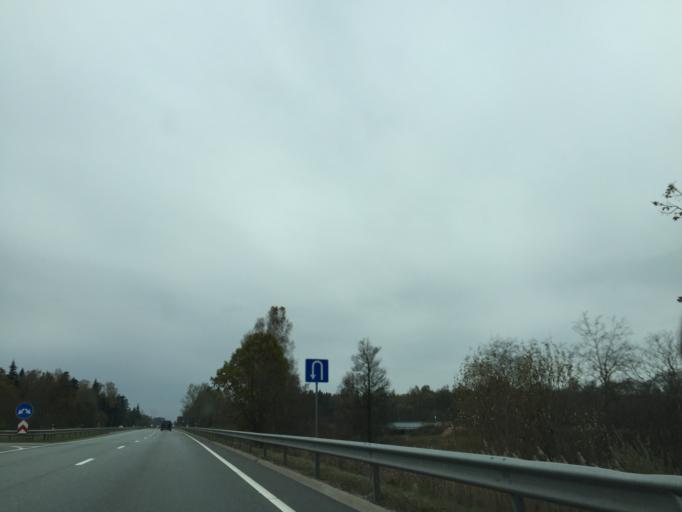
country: LV
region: Olaine
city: Olaine
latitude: 56.7395
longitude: 23.8742
